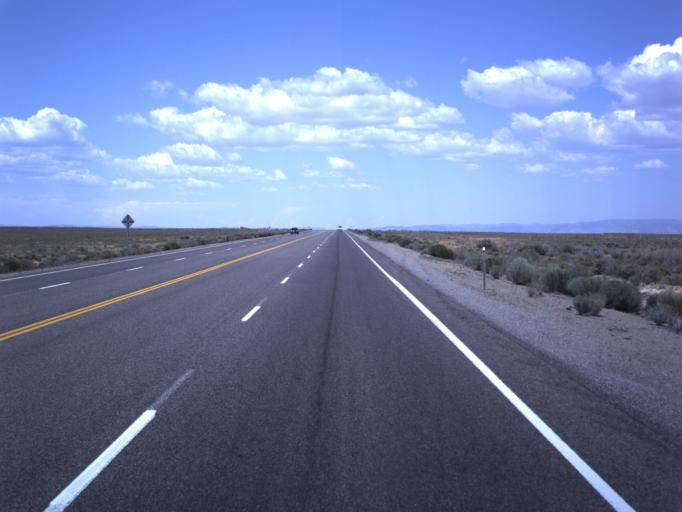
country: US
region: Utah
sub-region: Emery County
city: Huntington
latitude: 39.3968
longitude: -110.8941
